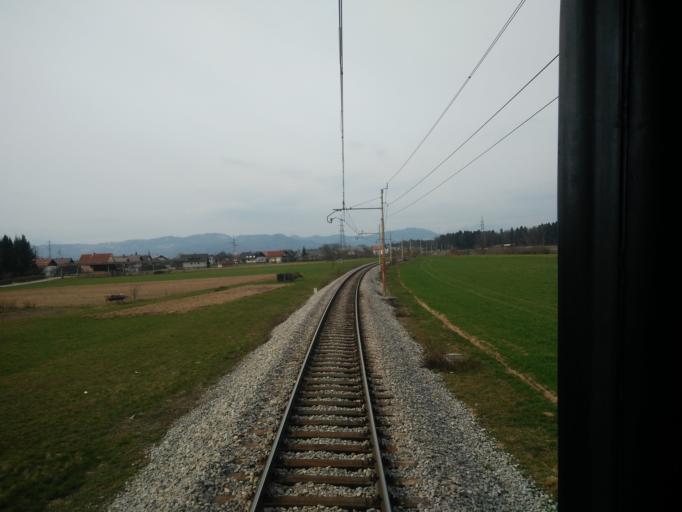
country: SI
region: Skofja Loka
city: Sv. Duh
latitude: 46.1611
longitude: 14.3615
